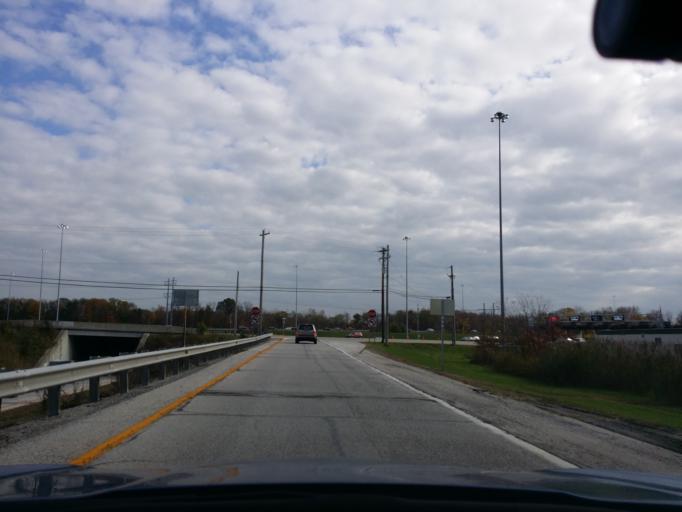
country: US
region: Ohio
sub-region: Cuyahoga County
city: Middleburg Heights
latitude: 41.3377
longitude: -81.8205
